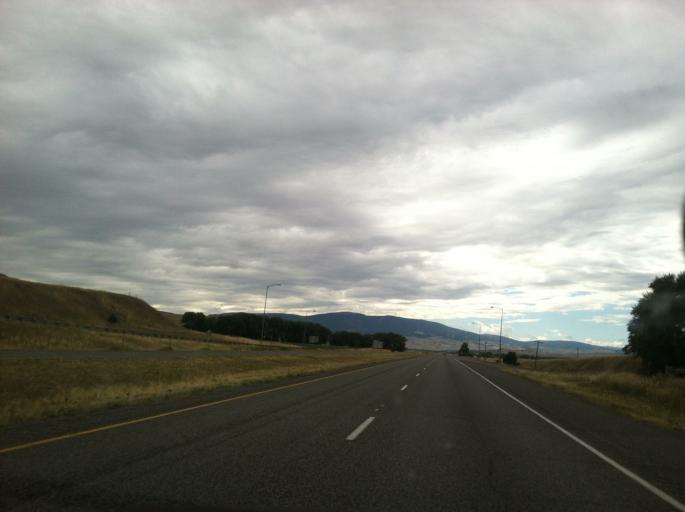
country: US
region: Montana
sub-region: Park County
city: Livingston
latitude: 45.7059
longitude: -110.4575
